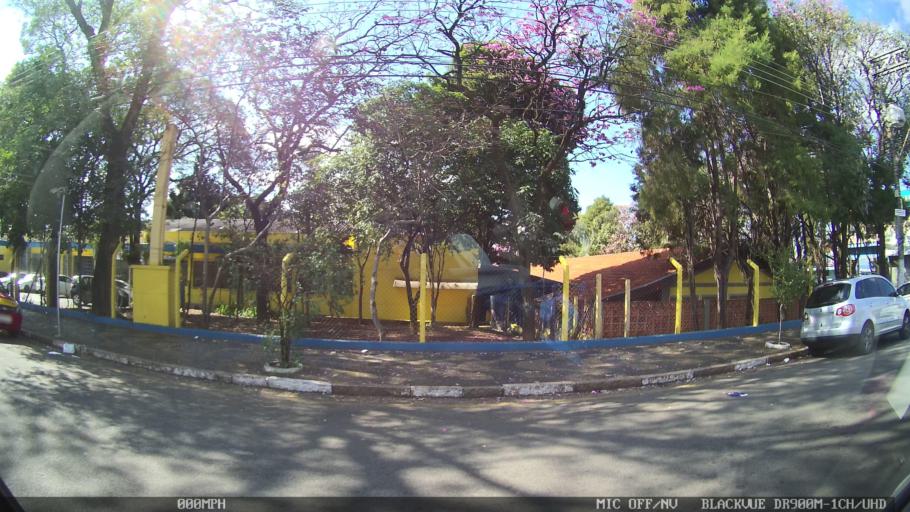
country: BR
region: Sao Paulo
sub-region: Sumare
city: Sumare
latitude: -22.8202
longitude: -47.2687
